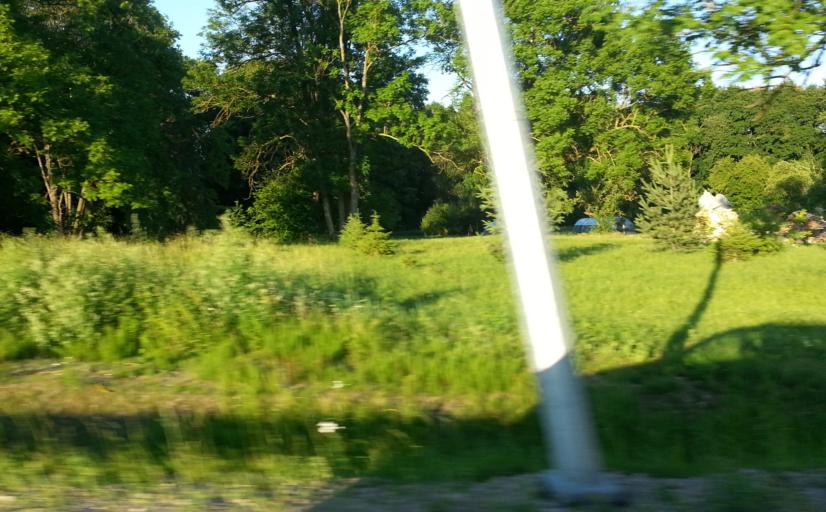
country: LT
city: Ramygala
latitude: 55.6190
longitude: 24.3478
